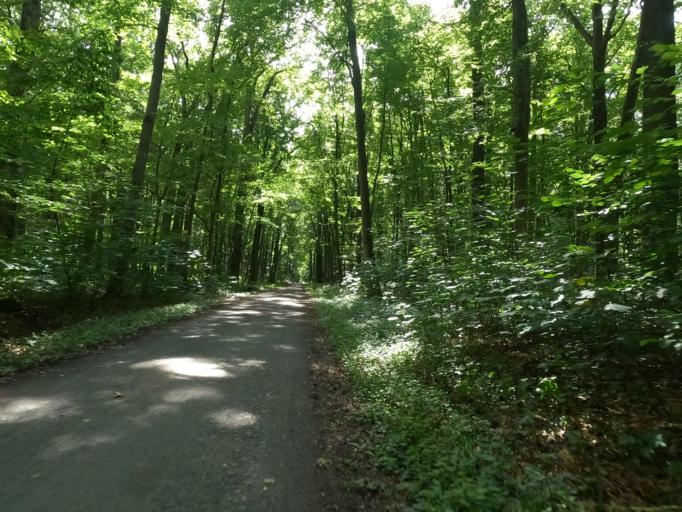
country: DE
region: Hesse
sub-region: Regierungsbezirk Darmstadt
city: Neu Isenburg
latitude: 50.0815
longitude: 8.7233
